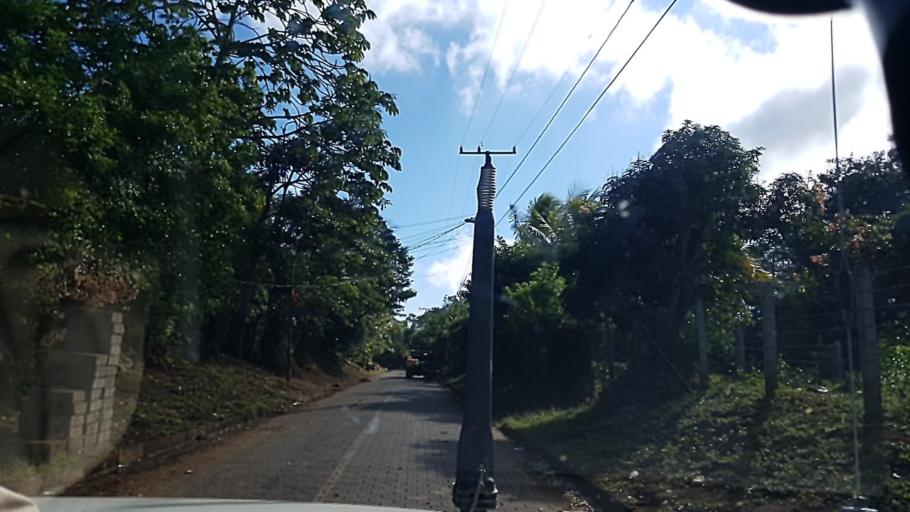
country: NI
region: Carazo
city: La Paz de Oriente
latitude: 11.8321
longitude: -86.1586
